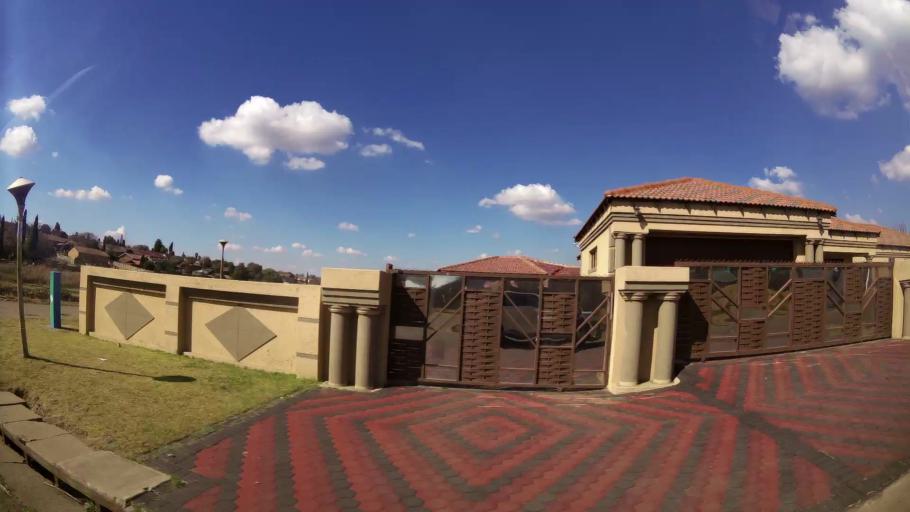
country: ZA
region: Mpumalanga
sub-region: Nkangala District Municipality
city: Witbank
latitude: -25.9362
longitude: 29.2451
